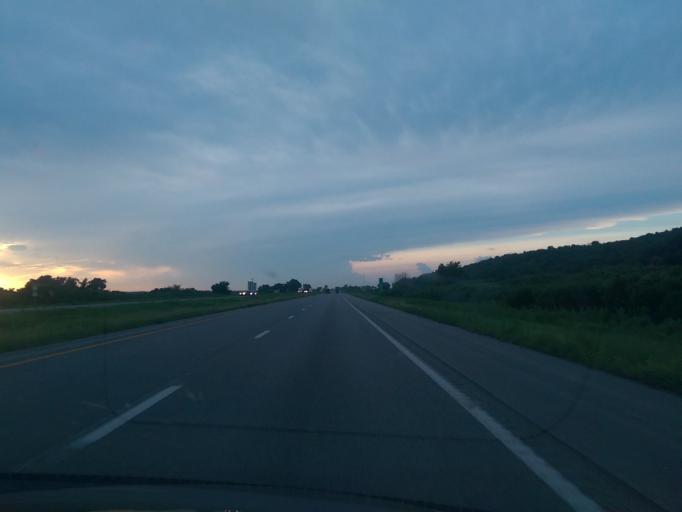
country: US
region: Missouri
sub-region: Atchison County
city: Rock Port
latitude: 40.2752
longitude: -95.4690
